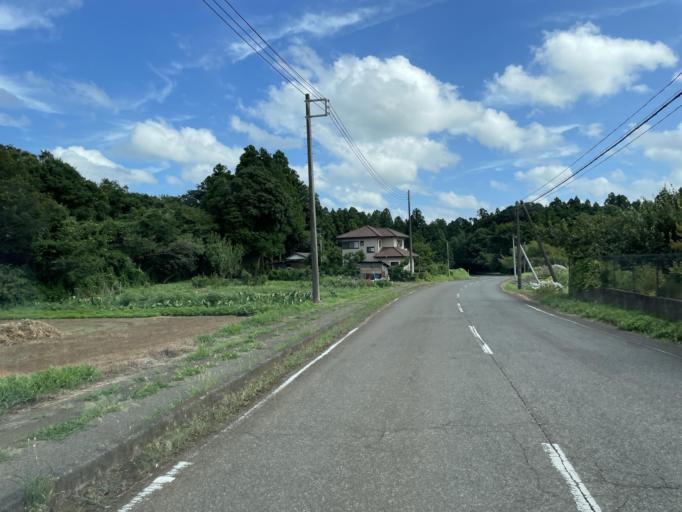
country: JP
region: Chiba
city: Sawara
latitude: 35.8068
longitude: 140.4666
